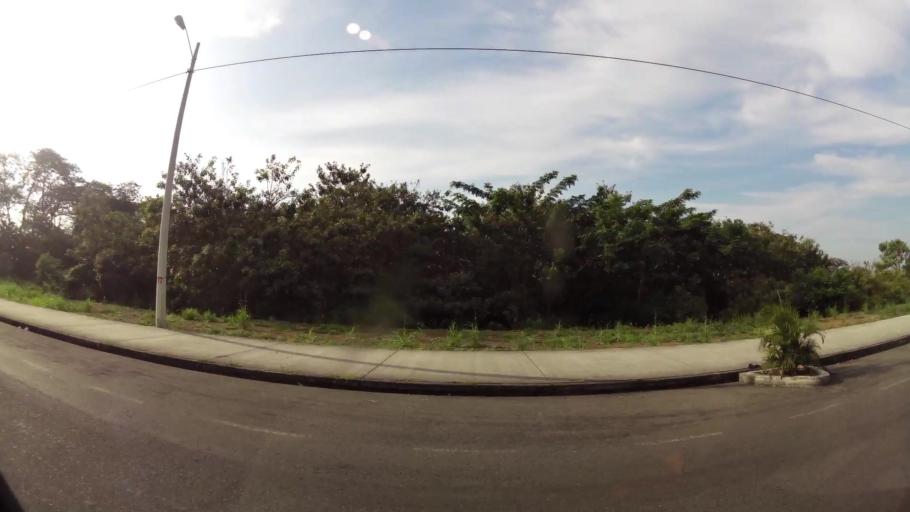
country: EC
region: Guayas
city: Eloy Alfaro
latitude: -2.0595
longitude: -79.8853
